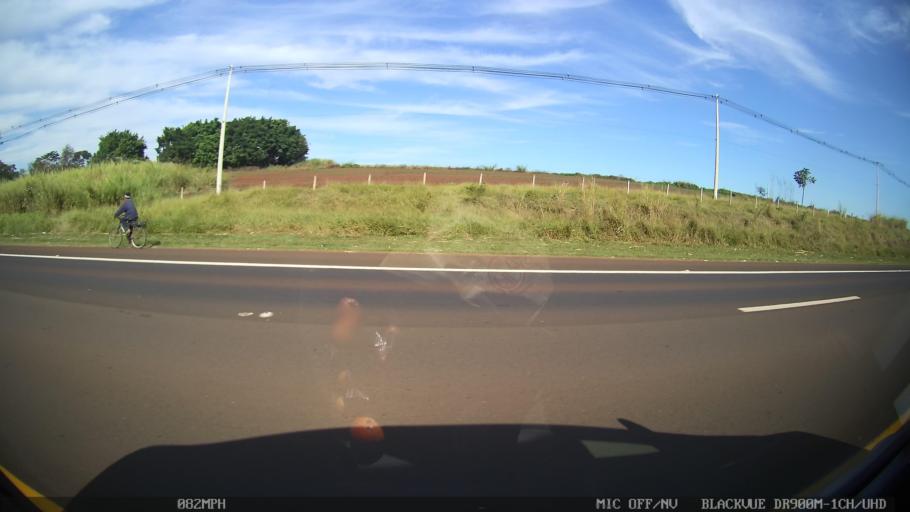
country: BR
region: Sao Paulo
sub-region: Americo Brasiliense
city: Americo Brasiliense
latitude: -21.7827
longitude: -48.1140
